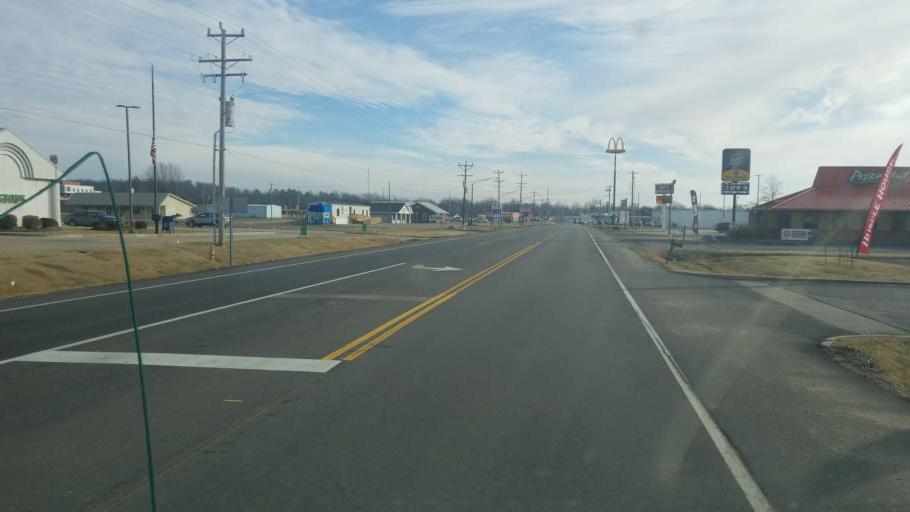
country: US
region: Missouri
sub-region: Stoddard County
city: Dexter
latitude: 36.8037
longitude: -89.9747
